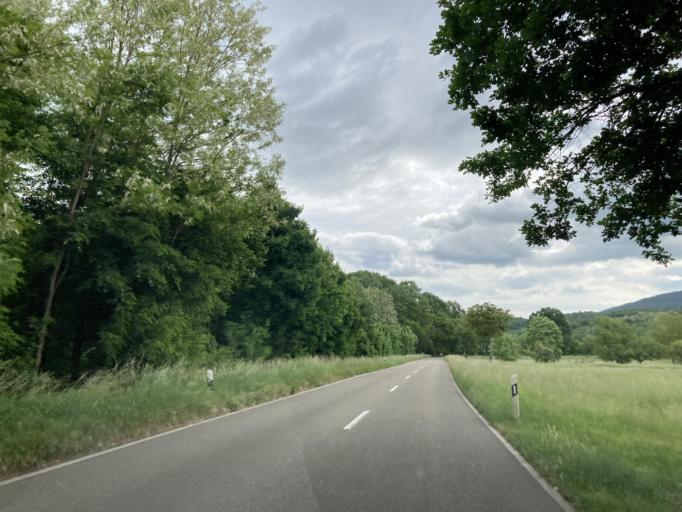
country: DE
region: Baden-Wuerttemberg
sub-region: Karlsruhe Region
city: Muggensturm
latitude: 48.8638
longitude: 8.2926
